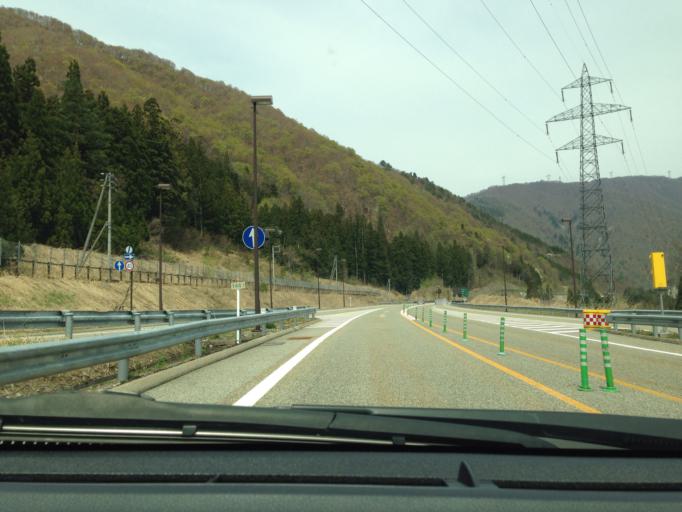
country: JP
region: Toyama
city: Fukumitsu
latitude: 36.2760
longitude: 136.8947
